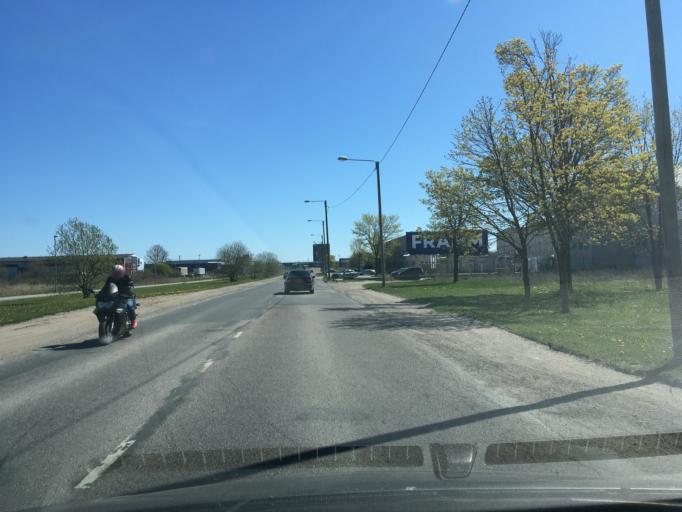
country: EE
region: Harju
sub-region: Joelaehtme vald
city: Loo
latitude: 59.4595
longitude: 24.9297
